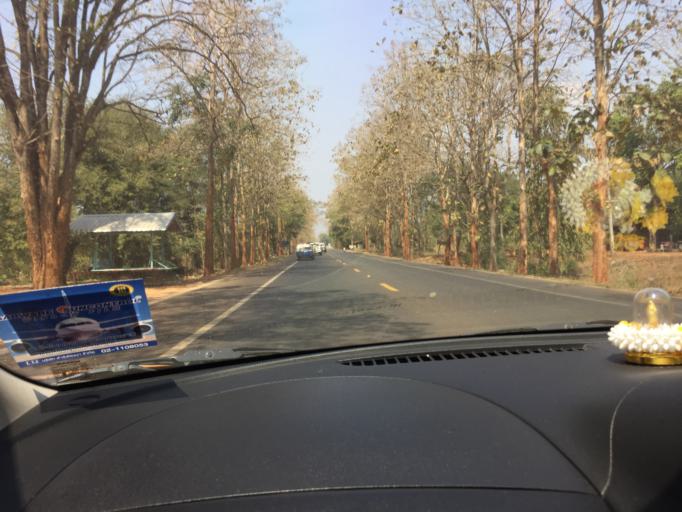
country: TH
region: Kanchanaburi
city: Sai Yok
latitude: 14.1698
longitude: 99.1316
